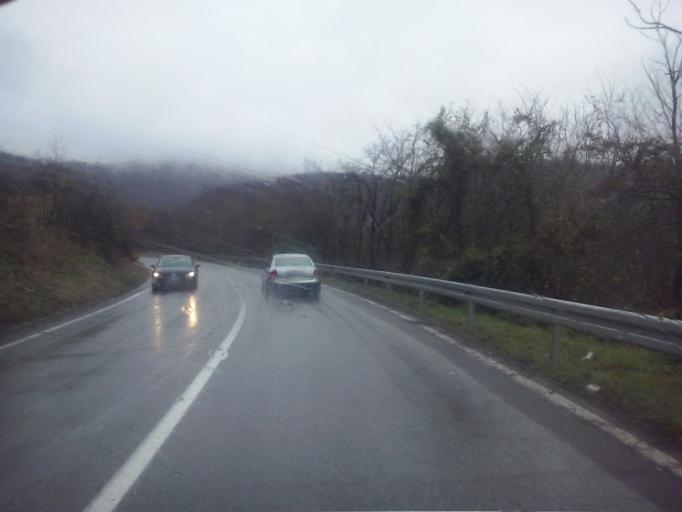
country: RS
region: Central Serbia
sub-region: Raski Okrug
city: Raska
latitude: 43.3429
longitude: 20.6434
